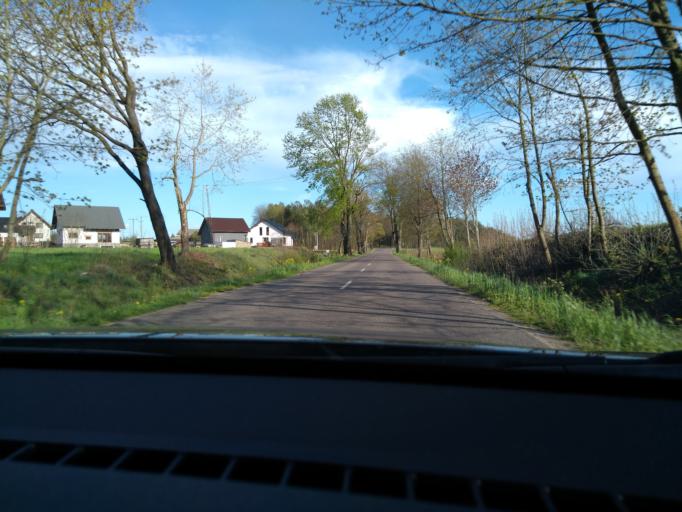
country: PL
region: Pomeranian Voivodeship
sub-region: Powiat kartuski
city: Suleczyno
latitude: 54.3320
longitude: 17.7720
